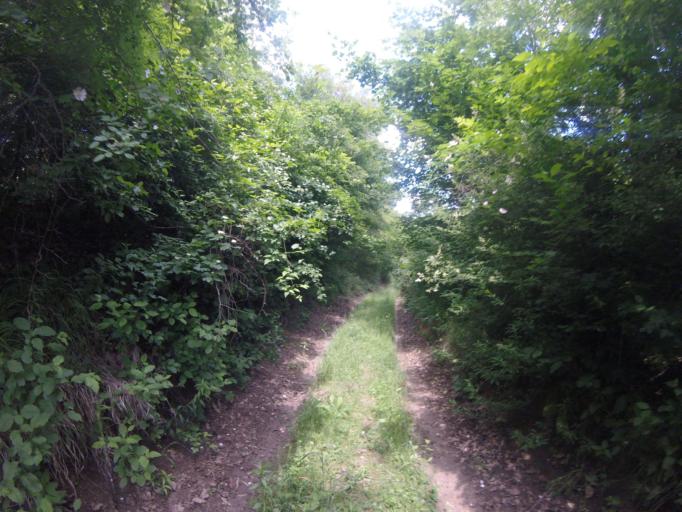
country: HU
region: Zala
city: Zalaszentgrot
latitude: 46.8959
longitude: 17.0355
